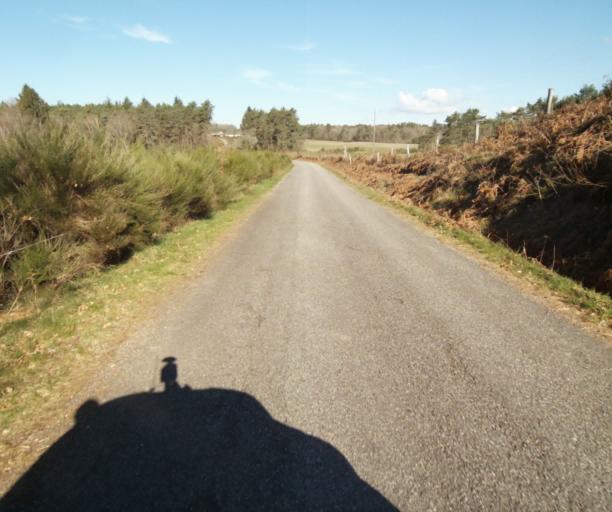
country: FR
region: Limousin
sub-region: Departement de la Correze
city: Correze
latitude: 45.2789
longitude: 1.9184
